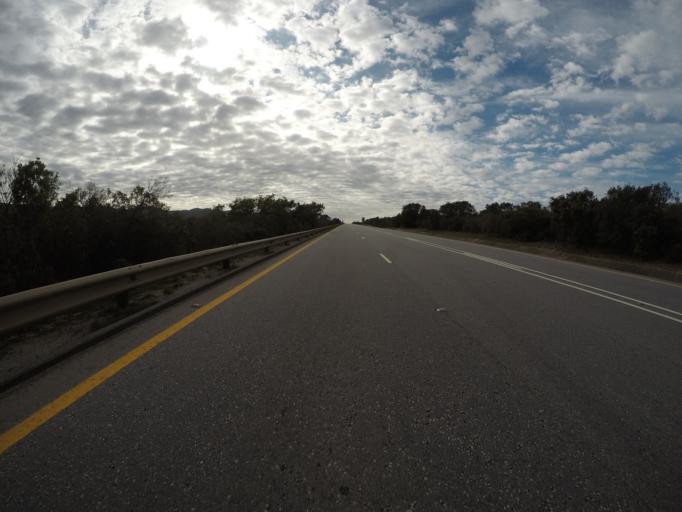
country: ZA
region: Eastern Cape
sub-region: Cacadu District Municipality
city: Kruisfontein
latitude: -34.0128
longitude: 24.6434
